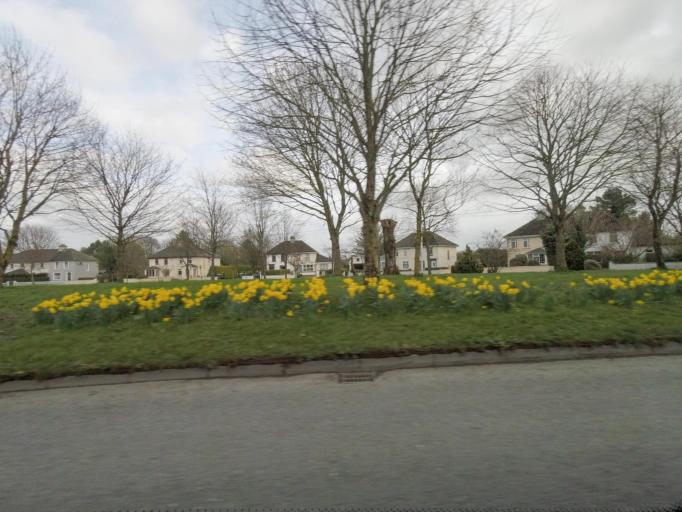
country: IE
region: Leinster
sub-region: Kildare
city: Kilcullen
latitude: 53.1259
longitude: -6.7498
